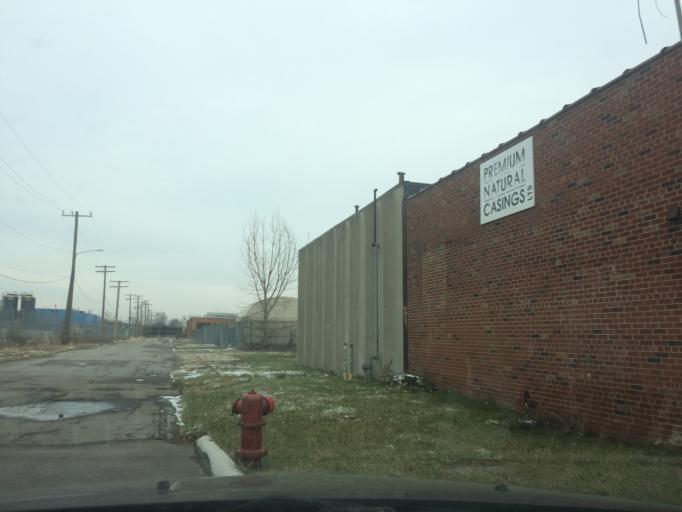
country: US
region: Michigan
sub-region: Wayne County
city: Hamtramck
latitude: 42.3648
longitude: -83.0506
